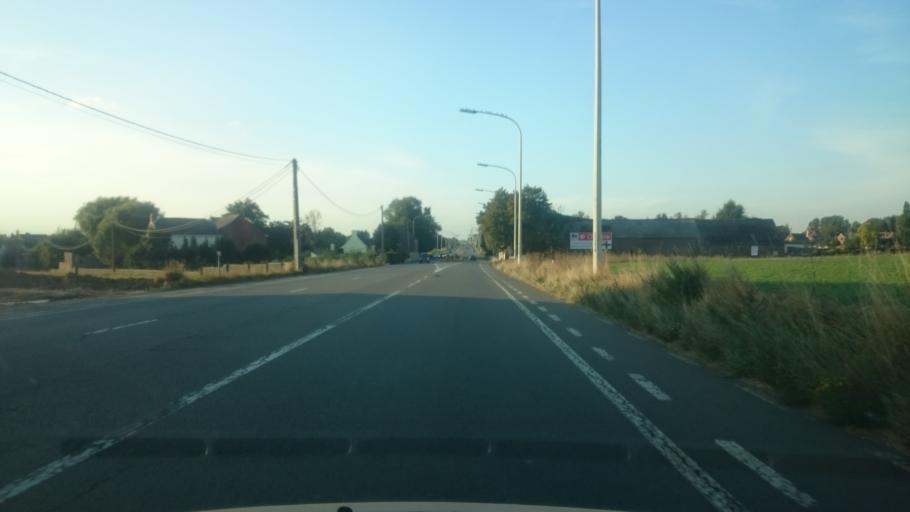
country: BE
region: Wallonia
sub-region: Province de Namur
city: Gembloux
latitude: 50.5890
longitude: 4.6810
